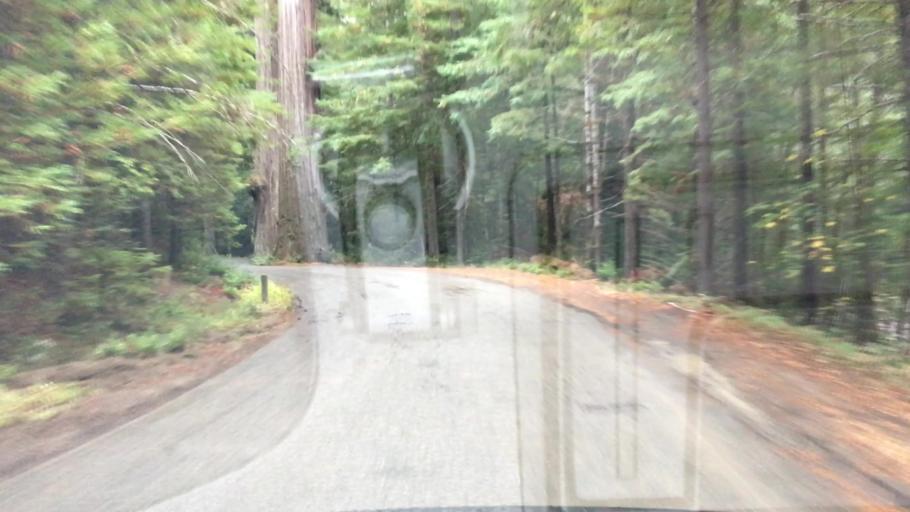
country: US
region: California
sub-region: Humboldt County
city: Rio Dell
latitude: 40.3525
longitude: -123.9835
